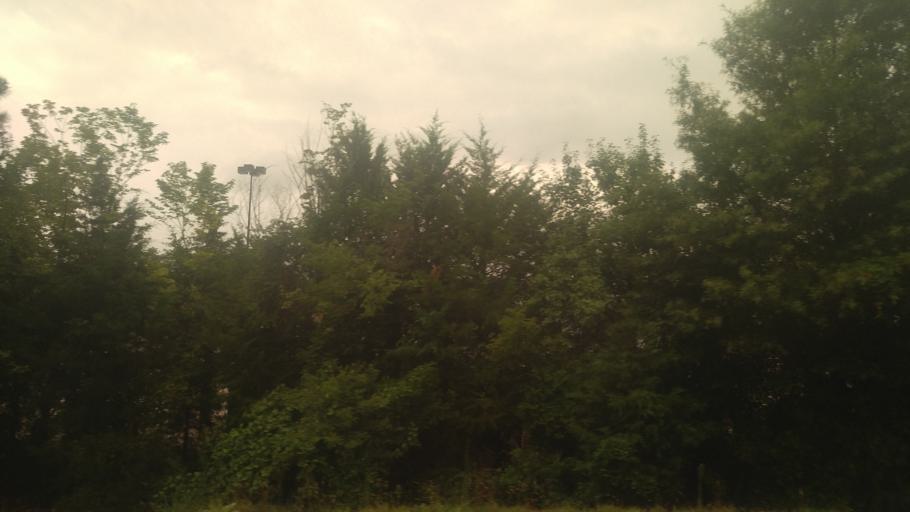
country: US
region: Virginia
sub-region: Henrico County
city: Dumbarton
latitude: 37.6145
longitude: -77.4948
